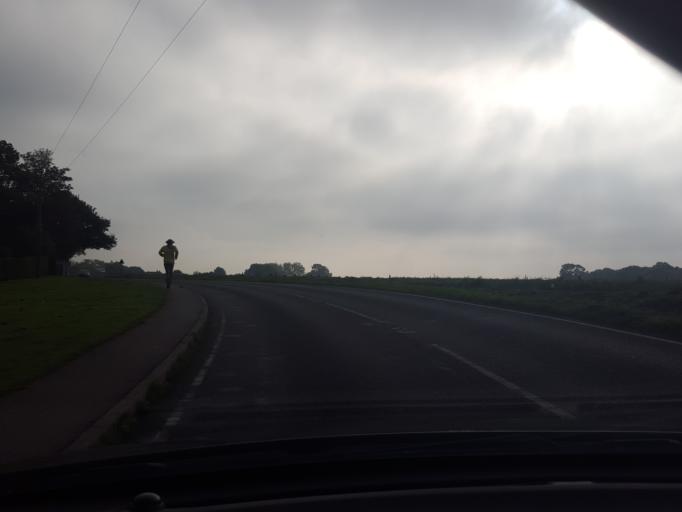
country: GB
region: England
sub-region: Essex
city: Mistley
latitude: 51.9382
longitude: 1.1128
